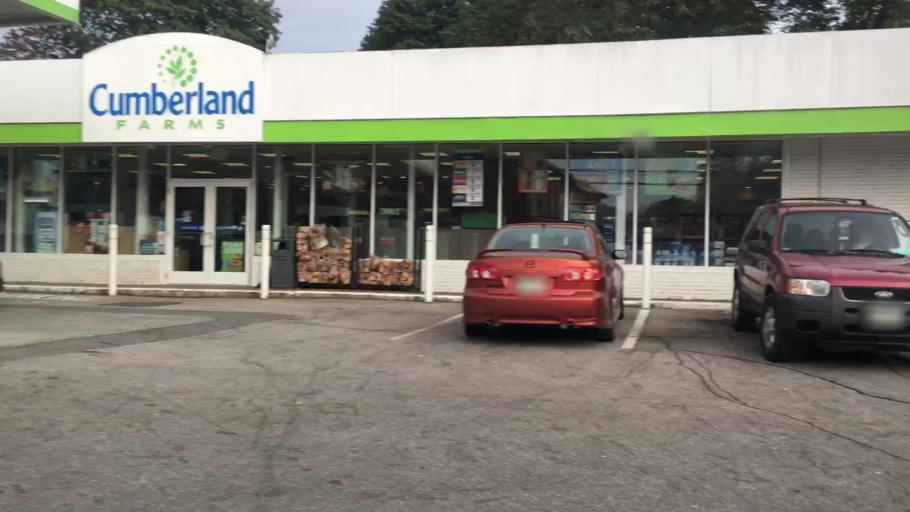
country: US
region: New Hampshire
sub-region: Strafford County
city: Rochester
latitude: 43.3342
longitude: -70.9403
